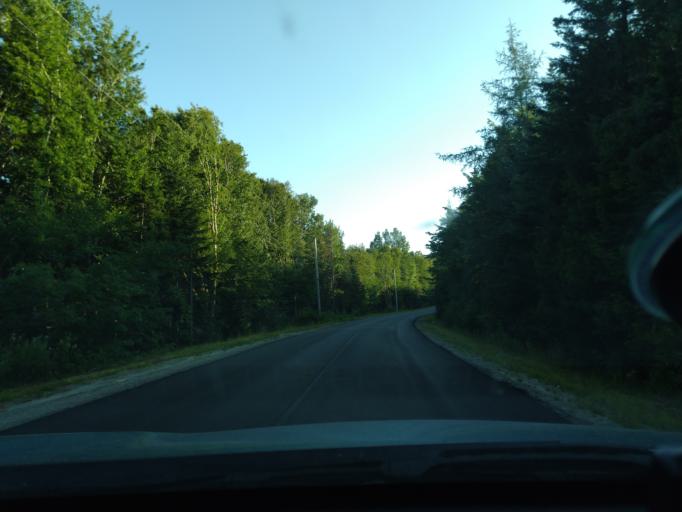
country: US
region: Maine
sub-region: Washington County
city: East Machias
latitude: 44.7035
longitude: -67.1518
